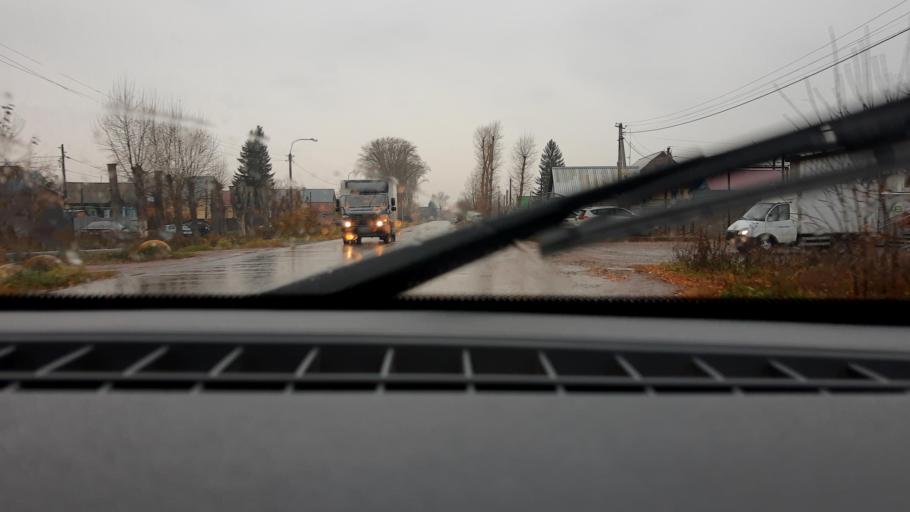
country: RU
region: Bashkortostan
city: Mikhaylovka
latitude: 54.7579
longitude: 55.9063
